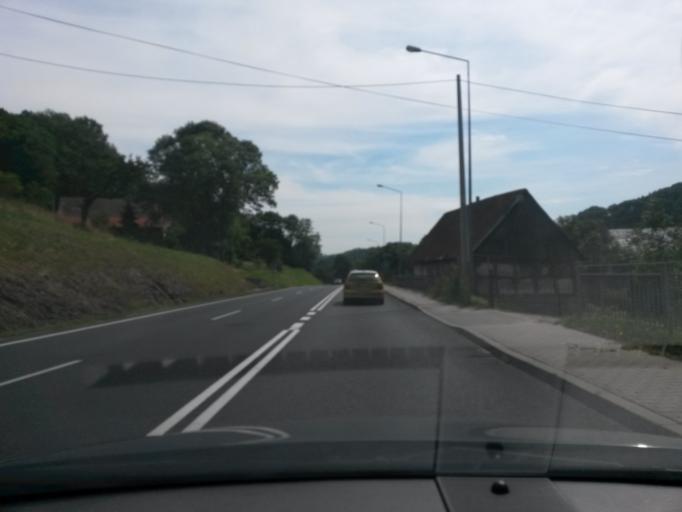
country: PL
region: Lower Silesian Voivodeship
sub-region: Powiat jeleniogorski
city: Janowice Wielkie
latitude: 50.9085
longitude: 15.9456
